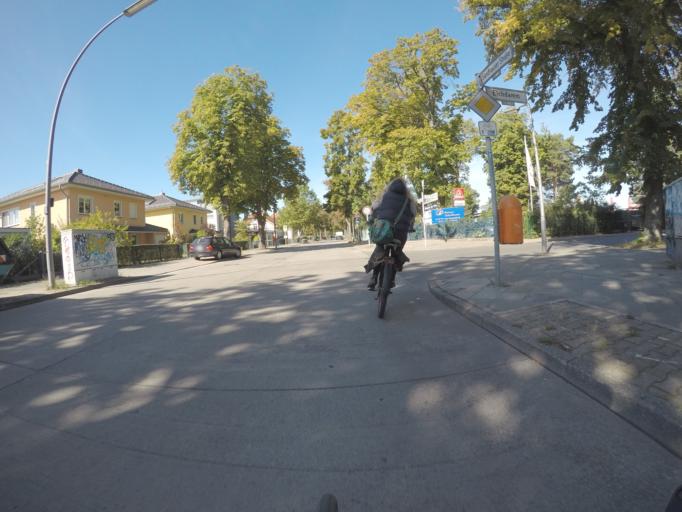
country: DE
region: Berlin
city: Konradshohe
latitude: 52.5996
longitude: 13.2135
